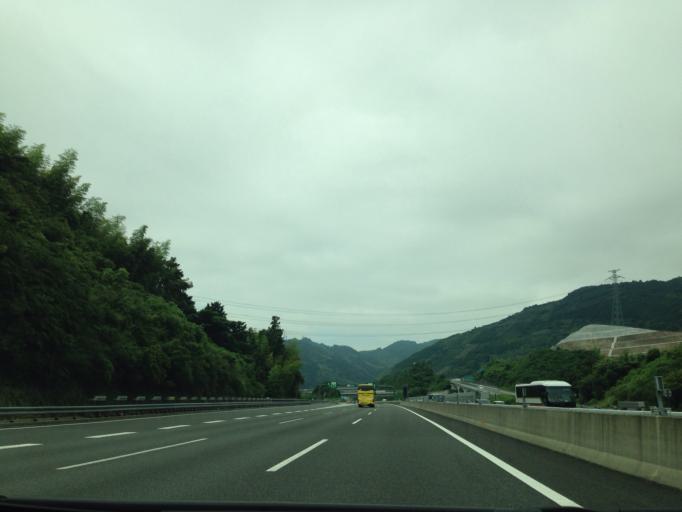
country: JP
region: Shizuoka
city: Shizuoka-shi
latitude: 35.0850
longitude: 138.4687
